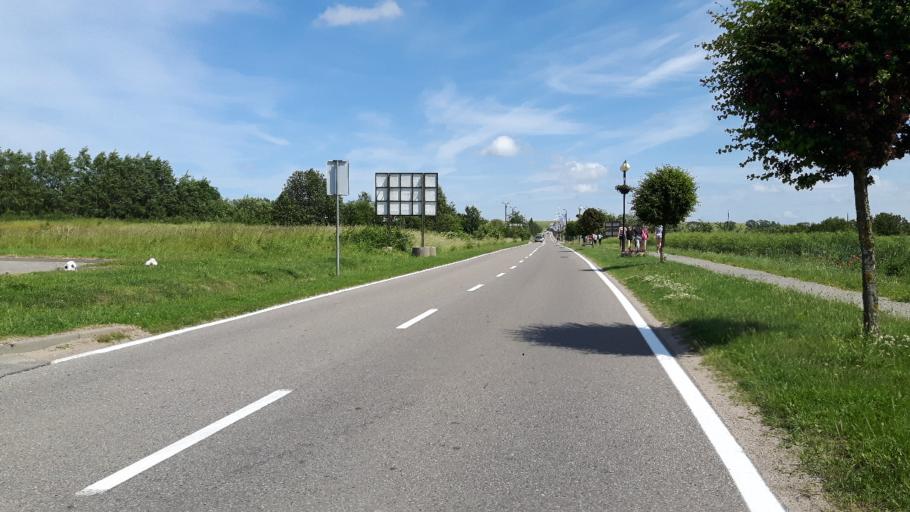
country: PL
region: Pomeranian Voivodeship
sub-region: Powiat wejherowski
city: Gniewino
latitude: 54.7158
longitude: 18.0309
